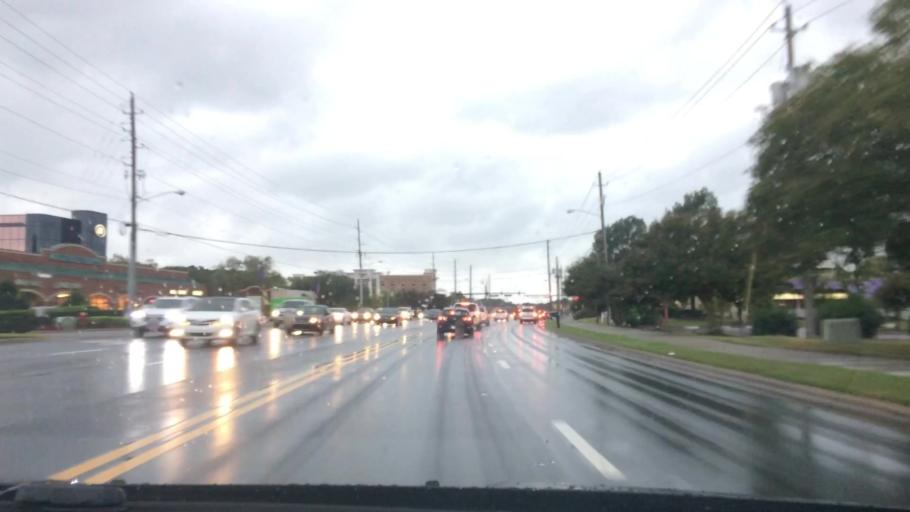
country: US
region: North Carolina
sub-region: Pitt County
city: Summerfield
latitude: 35.5744
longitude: -77.3877
